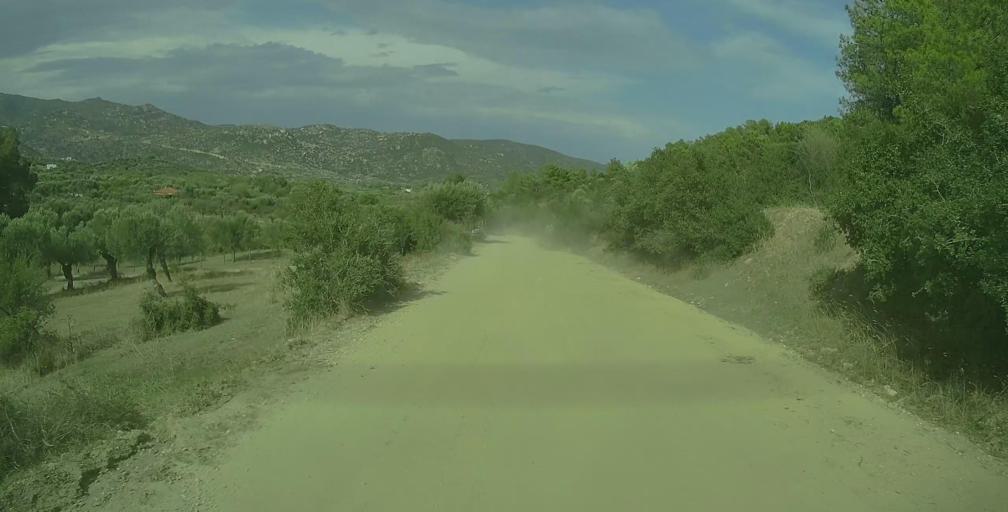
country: GR
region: Central Macedonia
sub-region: Nomos Chalkidikis
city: Sykia
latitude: 40.0248
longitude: 23.9459
